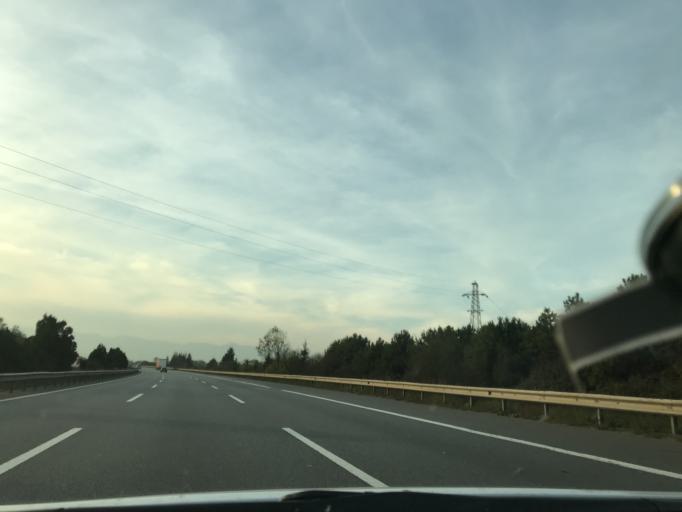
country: TR
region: Duzce
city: Cilimli
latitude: 40.8438
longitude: 31.0192
